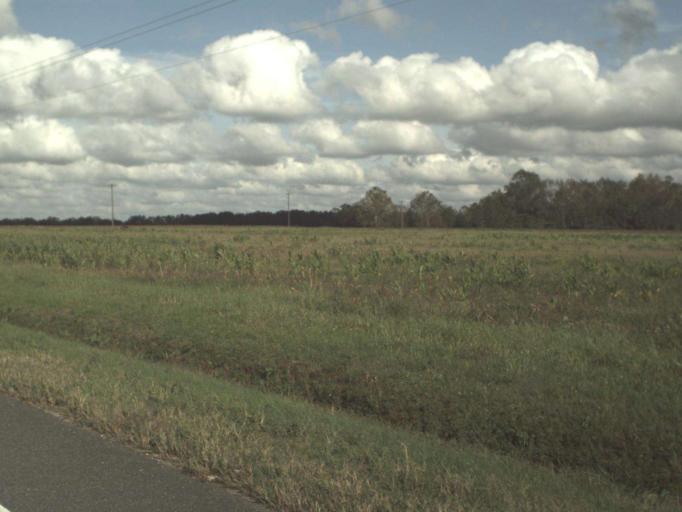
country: US
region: Alabama
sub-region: Escambia County
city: East Brewton
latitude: 30.9851
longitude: -87.0417
